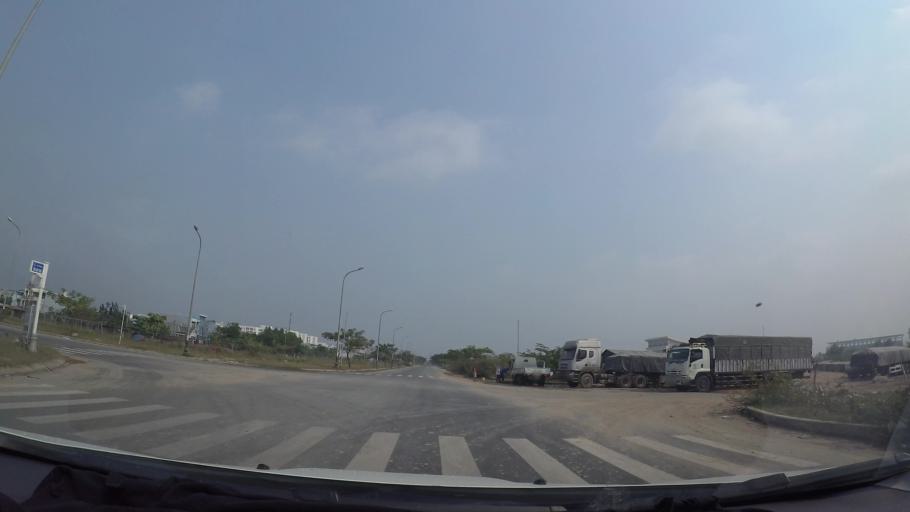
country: VN
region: Da Nang
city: Cam Le
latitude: 15.9947
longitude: 108.2163
